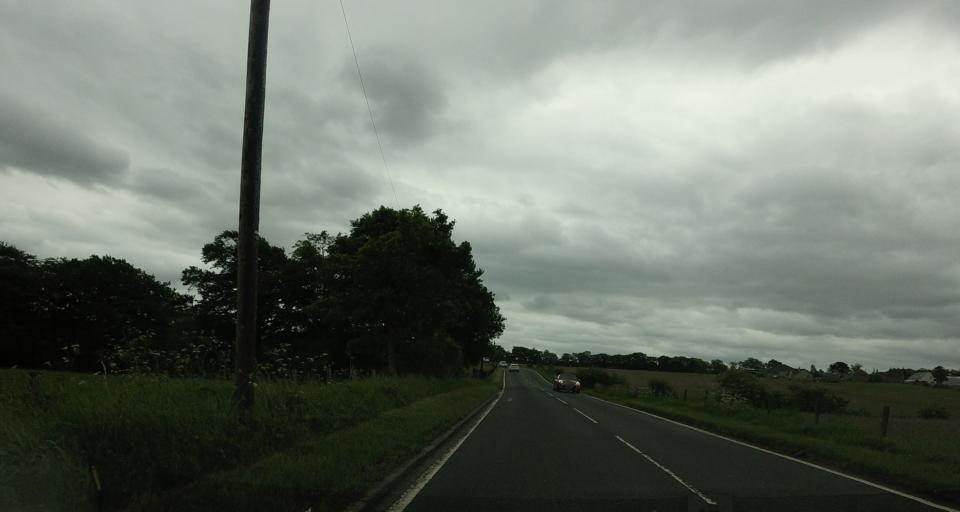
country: GB
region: Scotland
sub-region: Falkirk
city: Polmont
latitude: 55.9503
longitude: -3.6827
